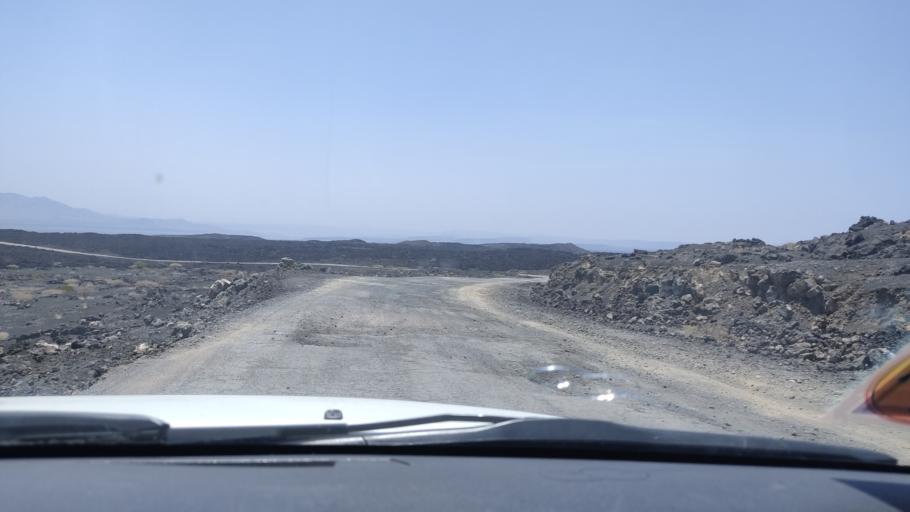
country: DJ
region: Tadjourah
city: Dorra
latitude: 12.3967
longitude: 42.1768
